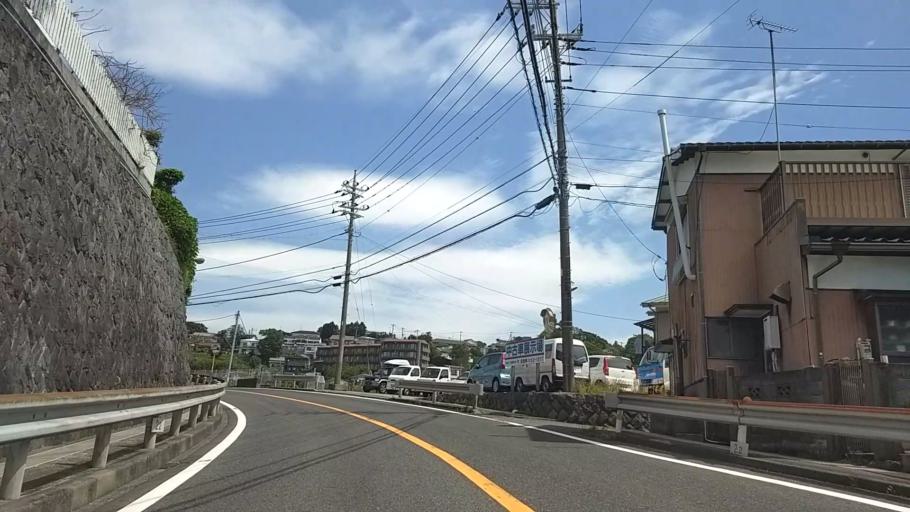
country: JP
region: Kanagawa
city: Yugawara
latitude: 35.1518
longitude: 139.1293
